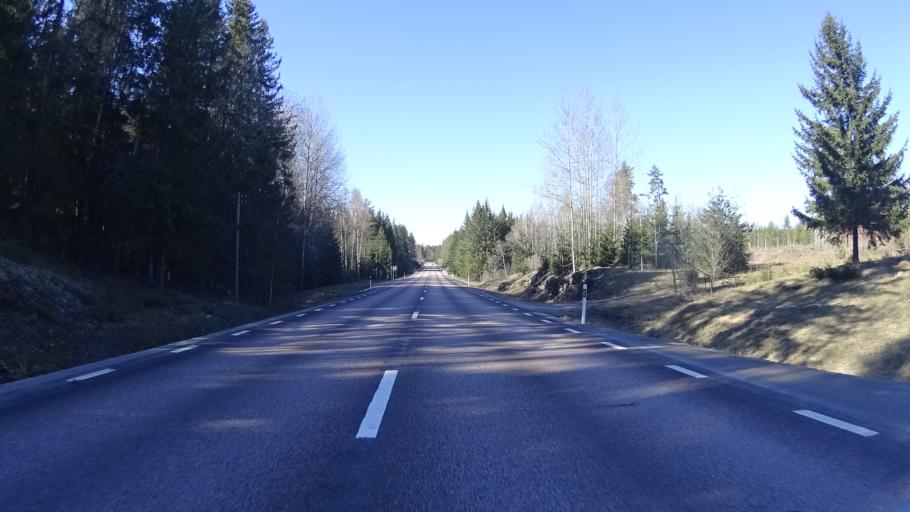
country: SE
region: Vaermland
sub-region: Karlstads Kommun
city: Edsvalla
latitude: 59.5985
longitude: 13.0034
